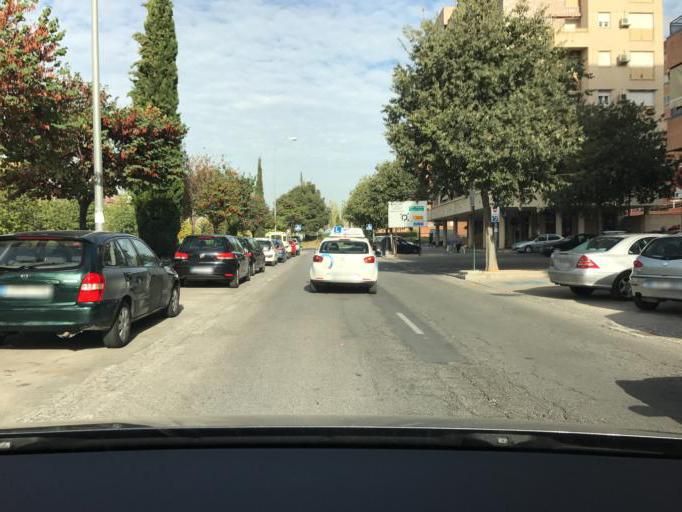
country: ES
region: Andalusia
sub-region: Provincia de Granada
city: Granada
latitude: 37.1989
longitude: -3.6160
